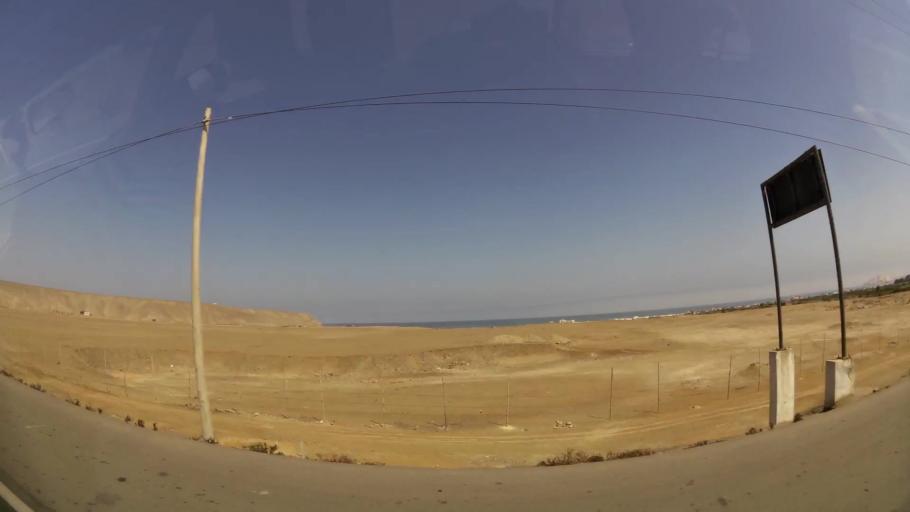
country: PE
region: Lima
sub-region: Provincia de Canete
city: Asia
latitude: -12.7980
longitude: -76.5539
